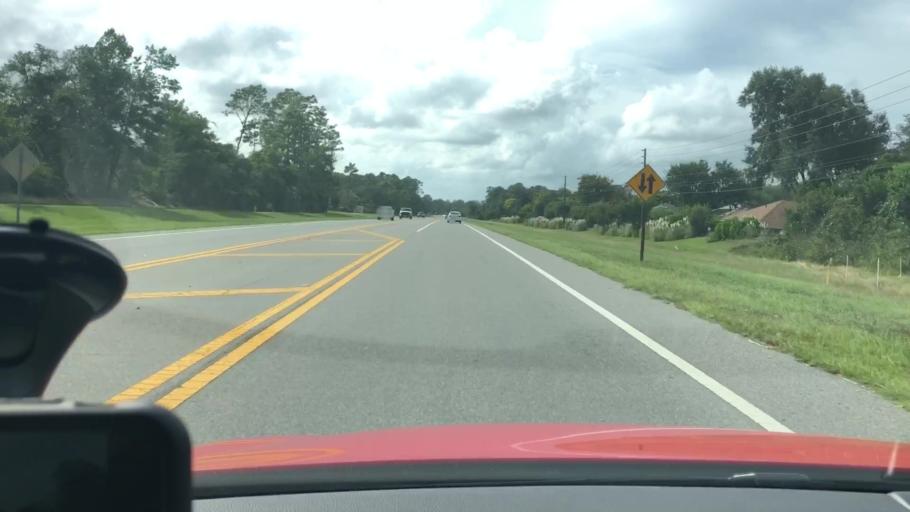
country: US
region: Florida
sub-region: Volusia County
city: Ormond Beach
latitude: 29.2617
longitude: -81.0863
